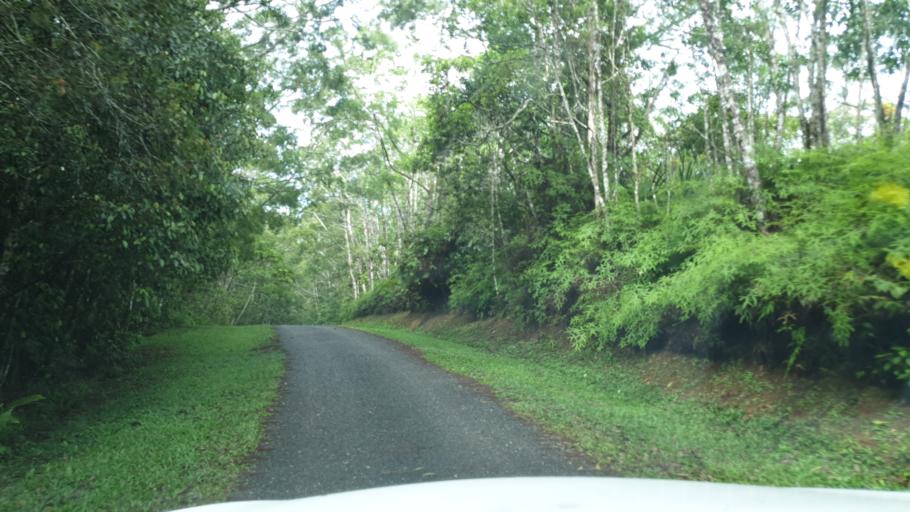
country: PG
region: National Capital
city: Port Moresby
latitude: -9.4336
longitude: 147.3676
